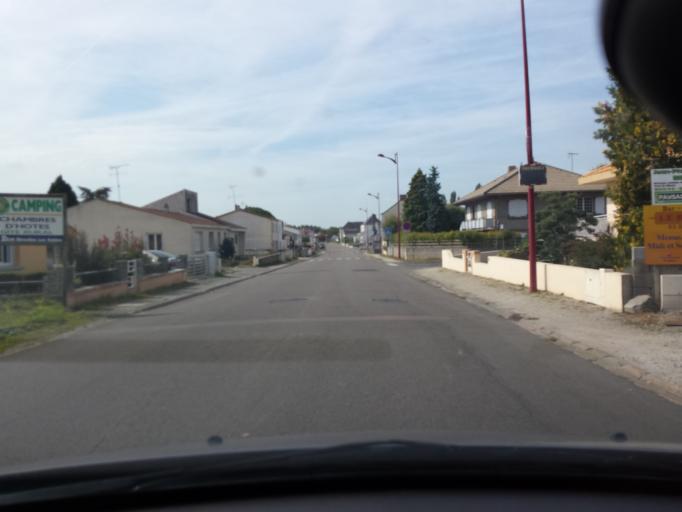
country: FR
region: Pays de la Loire
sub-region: Departement de la Vendee
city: Nieul-le-Dolent
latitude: 46.5753
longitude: -1.5021
